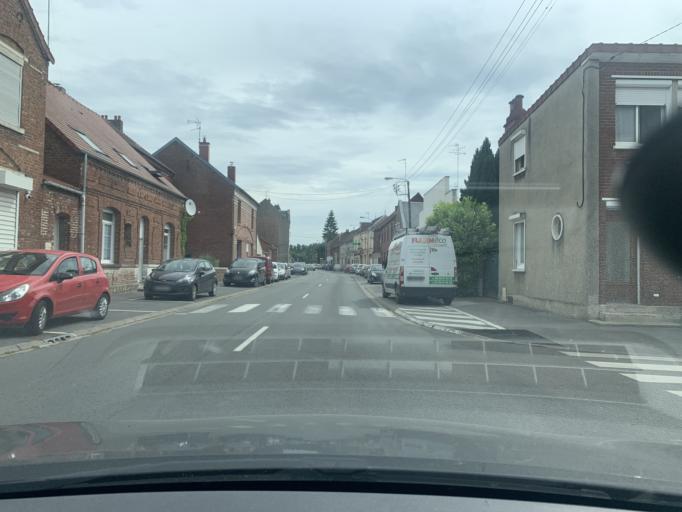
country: FR
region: Nord-Pas-de-Calais
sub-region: Departement du Nord
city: Marcoing
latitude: 50.1221
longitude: 3.1749
